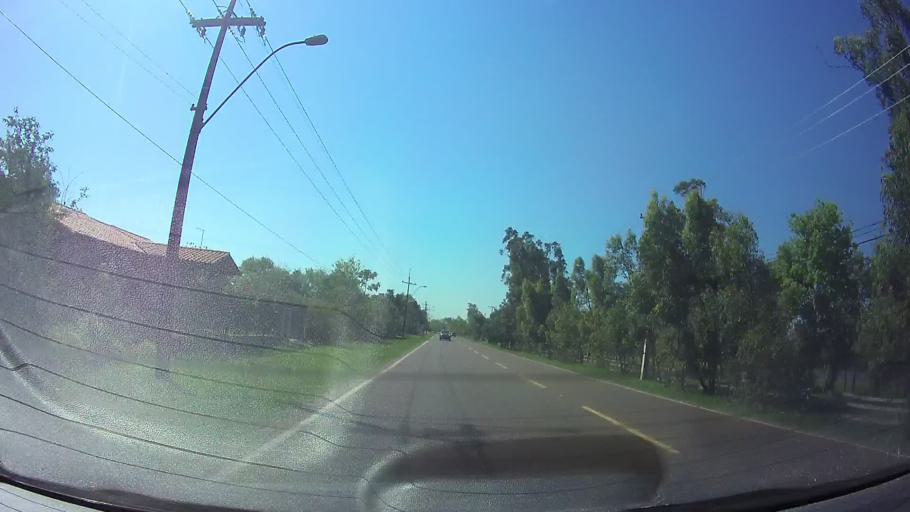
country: PY
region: Central
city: Ypacarai
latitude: -25.3586
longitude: -57.2664
